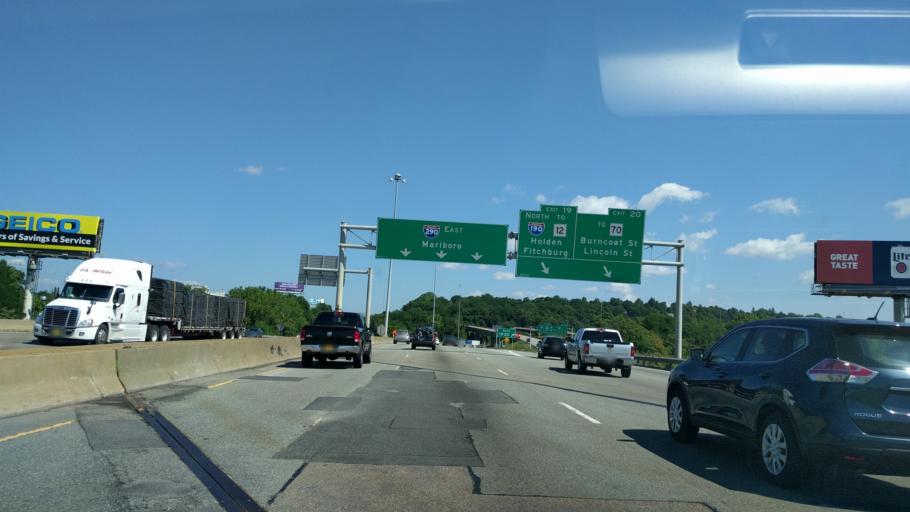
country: US
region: Massachusetts
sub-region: Worcester County
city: Worcester
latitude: 42.2838
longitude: -71.7978
